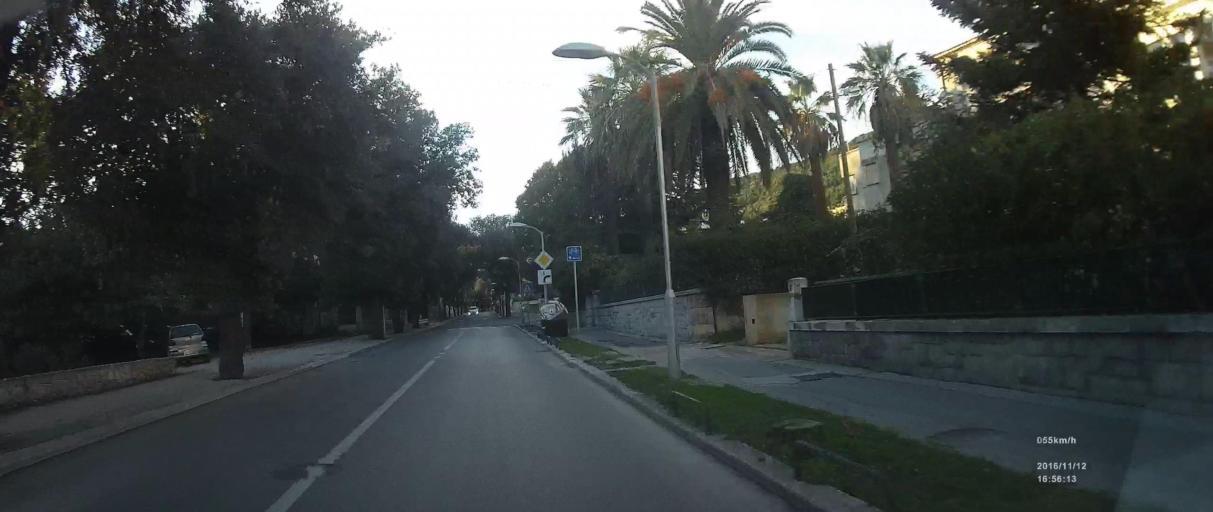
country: HR
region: Splitsko-Dalmatinska
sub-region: Grad Split
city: Split
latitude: 43.5037
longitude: 16.4243
